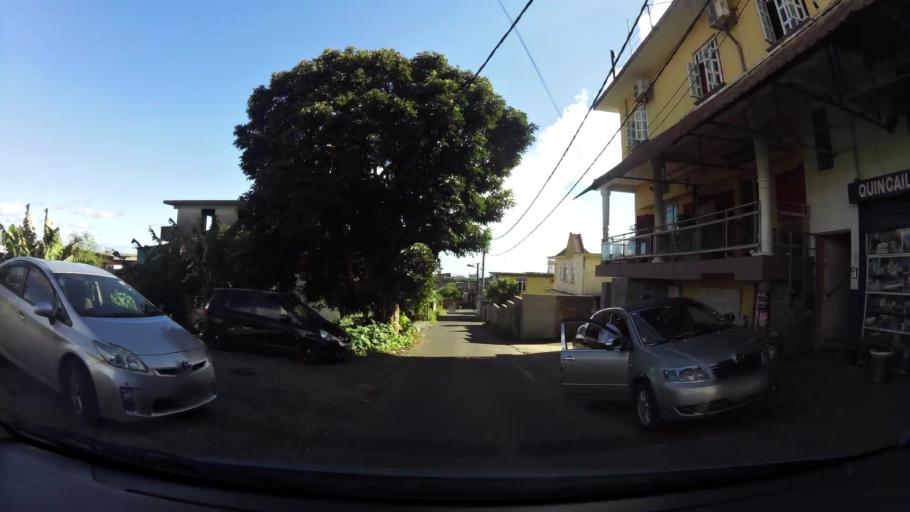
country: MU
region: Plaines Wilhems
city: Curepipe
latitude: -20.3048
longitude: 57.5121
